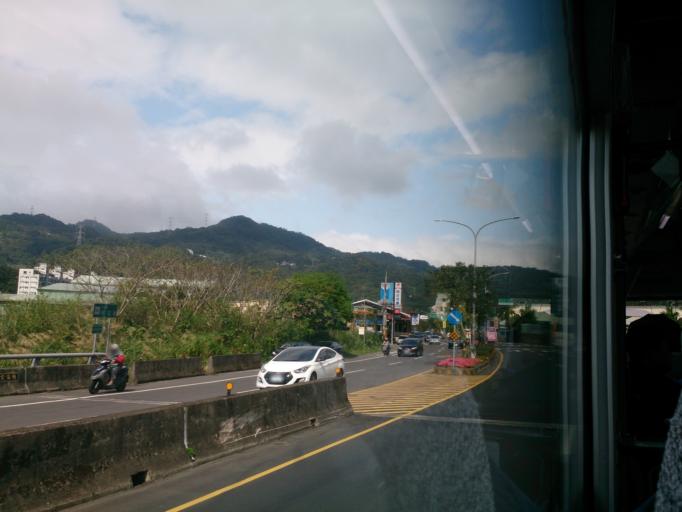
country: TW
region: Taipei
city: Taipei
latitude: 25.0047
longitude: 121.6303
